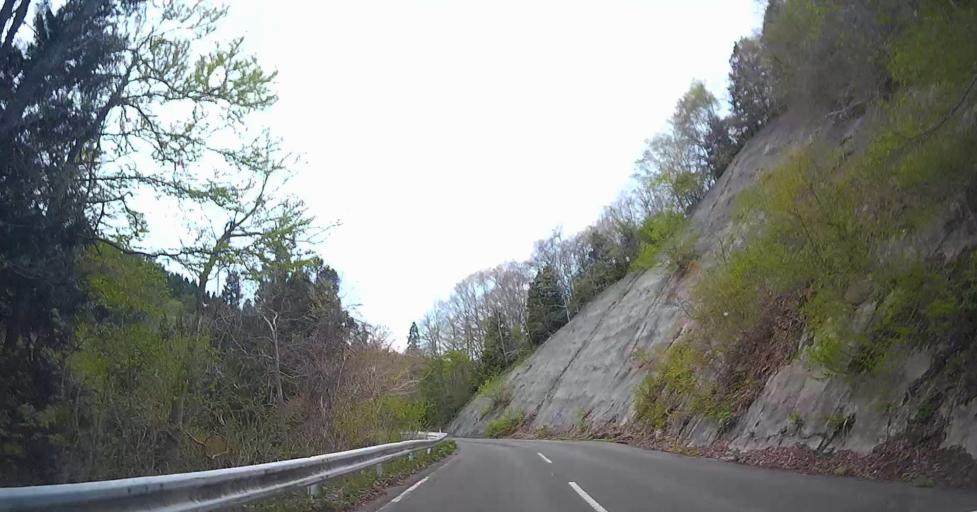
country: JP
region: Aomori
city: Goshogawara
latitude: 40.9052
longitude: 140.5329
